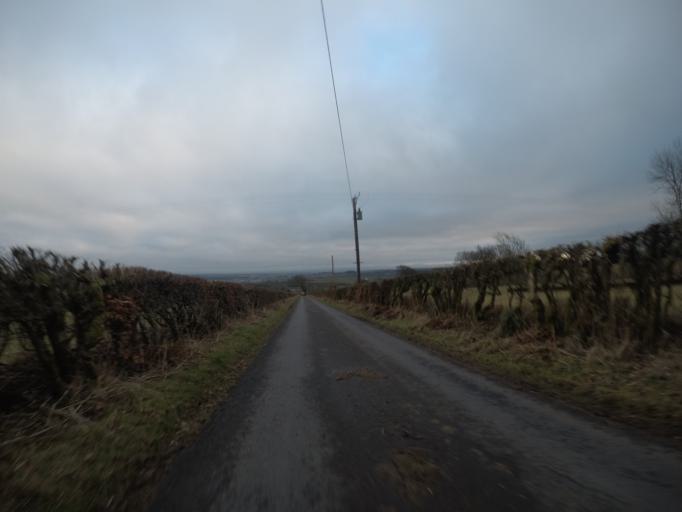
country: GB
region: Scotland
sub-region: North Ayrshire
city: Dalry
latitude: 55.7193
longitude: -4.7591
